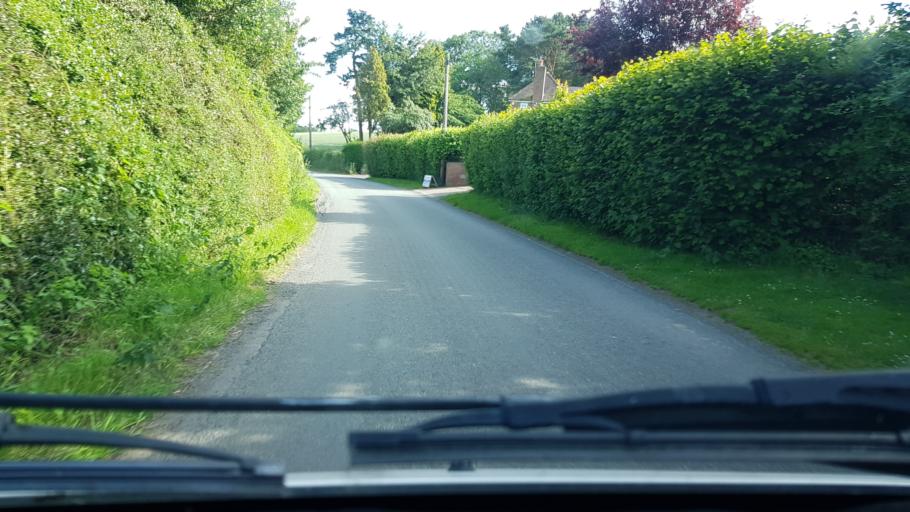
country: GB
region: England
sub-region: Worcestershire
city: Bewdley
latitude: 52.3586
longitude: -2.3284
